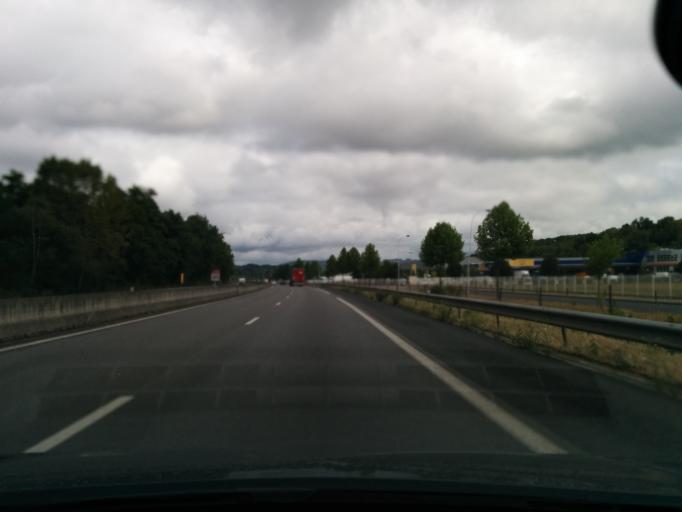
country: FR
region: Limousin
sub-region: Departement de la Correze
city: Ussac
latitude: 45.1770
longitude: 1.4904
